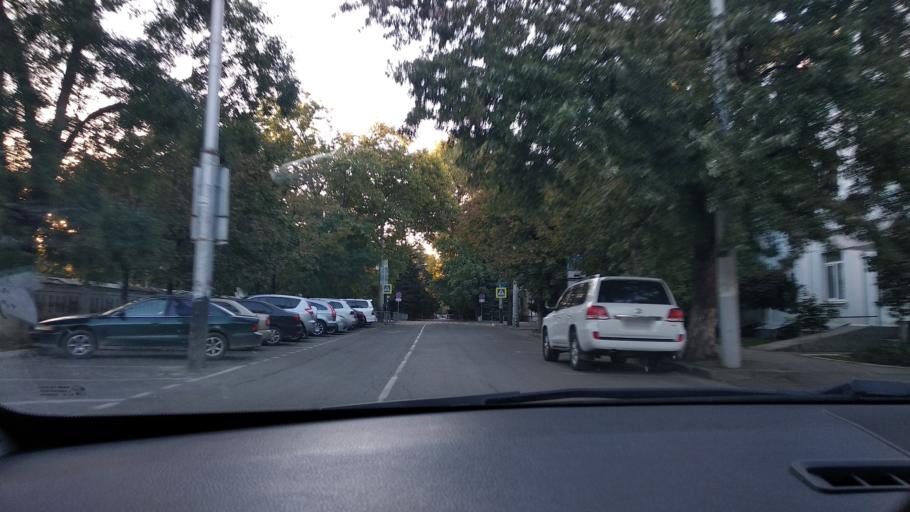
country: RU
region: Krasnodarskiy
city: Krasnodar
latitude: 45.0158
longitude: 38.9706
